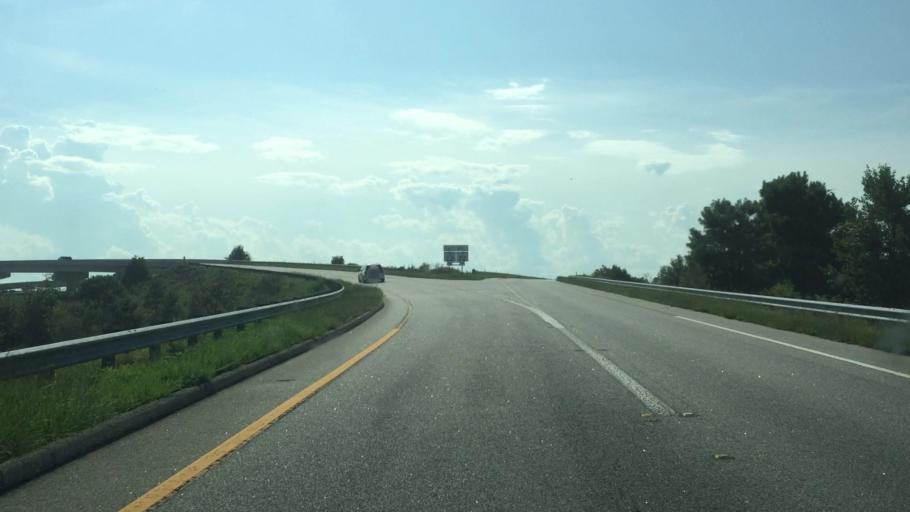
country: US
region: South Carolina
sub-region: Horry County
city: North Myrtle Beach
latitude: 33.8121
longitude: -78.7756
